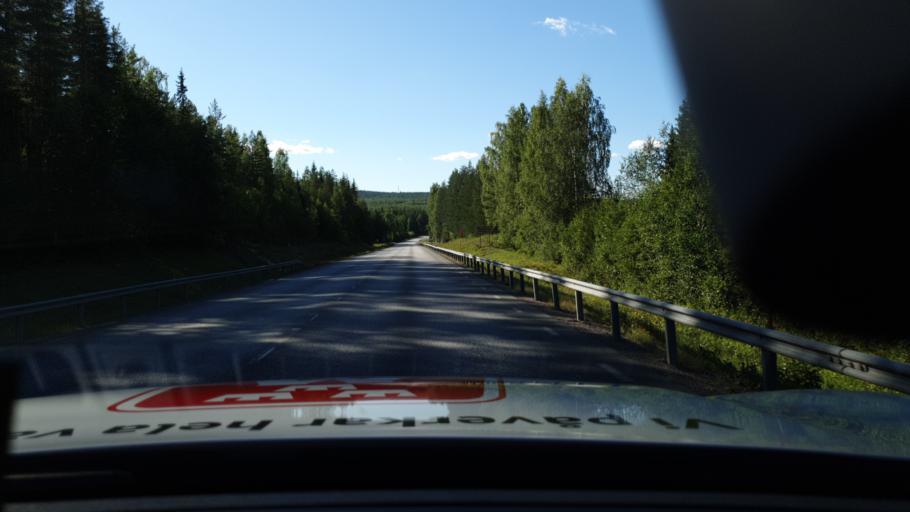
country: SE
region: Norrbotten
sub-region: Pitea Kommun
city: Norrfjarden
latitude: 65.6186
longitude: 21.4207
